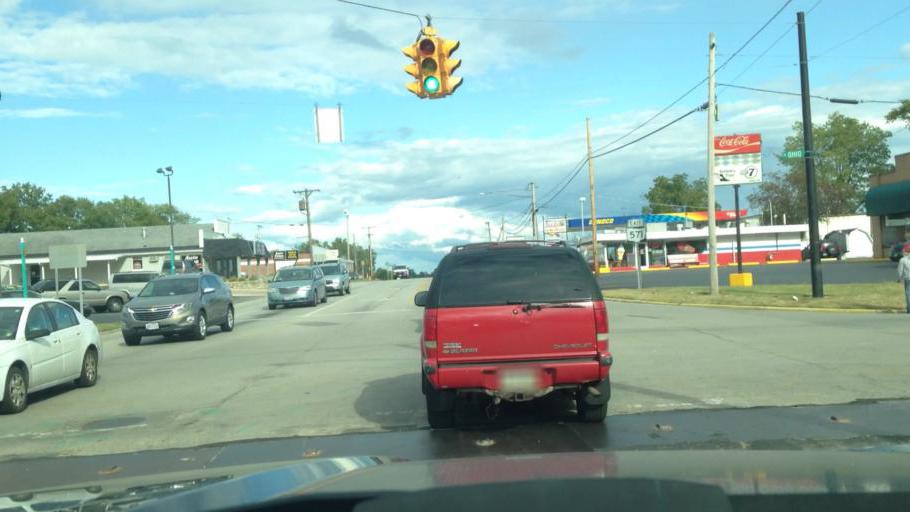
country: US
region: Ohio
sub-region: Darke County
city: Greenville
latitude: 40.0976
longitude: -84.6188
